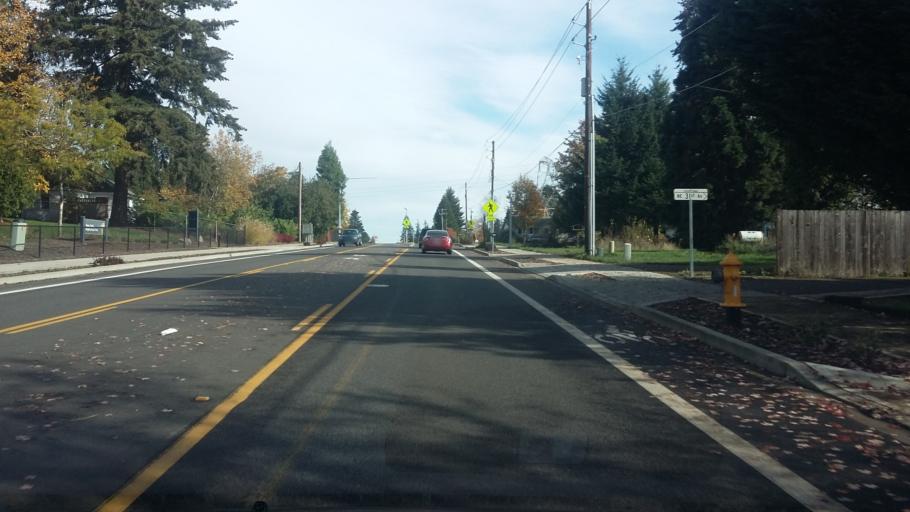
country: US
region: Washington
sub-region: Clark County
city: Salmon Creek
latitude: 45.6859
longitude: -122.6394
